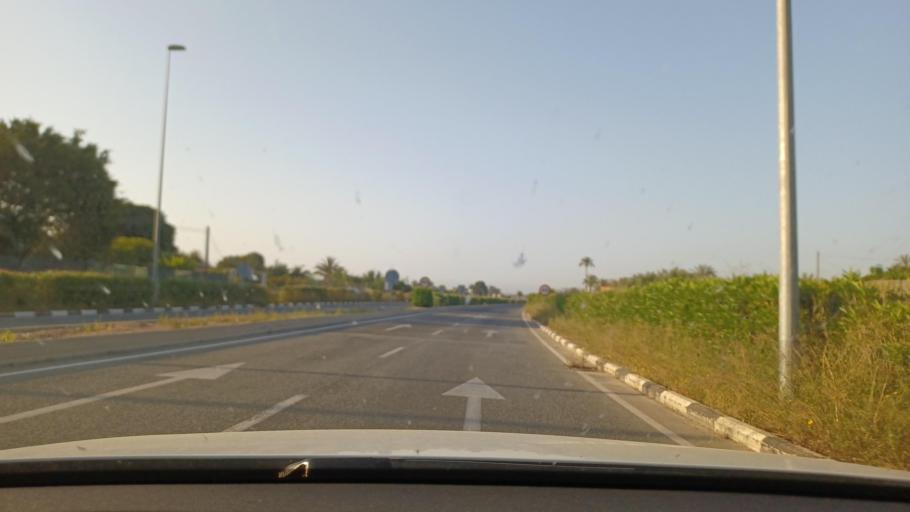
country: ES
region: Valencia
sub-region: Provincia de Alicante
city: Elche
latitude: 38.2315
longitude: -0.7000
